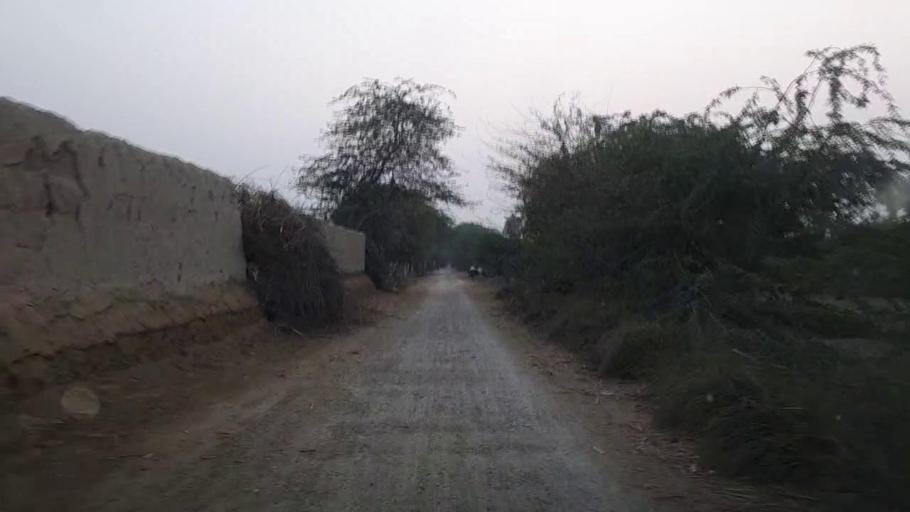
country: PK
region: Sindh
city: Kandiari
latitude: 26.9679
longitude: 68.4707
